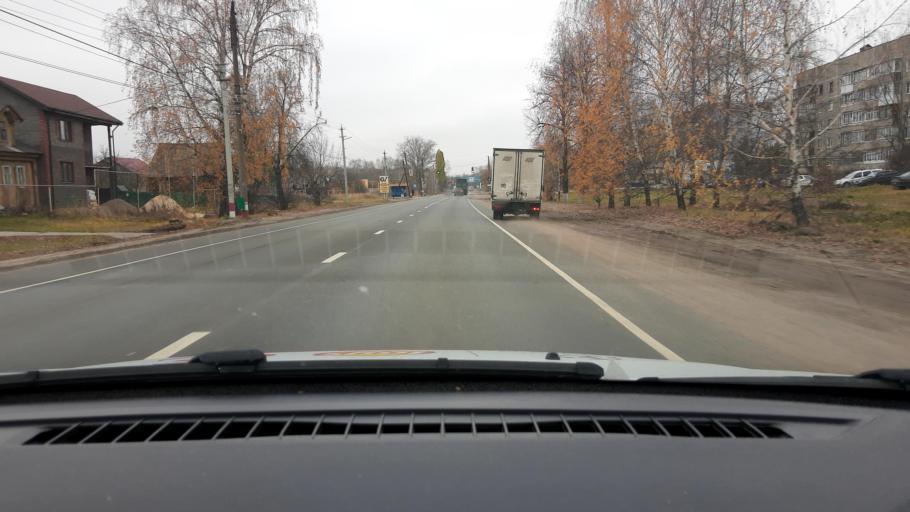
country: RU
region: Nizjnij Novgorod
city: Novaya Balakhna
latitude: 56.5184
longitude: 43.5780
